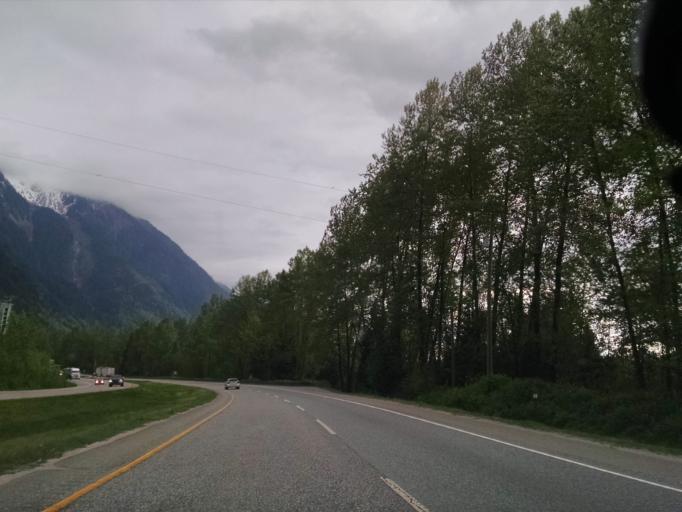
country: CA
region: British Columbia
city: Agassiz
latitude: 49.2388
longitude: -121.6802
